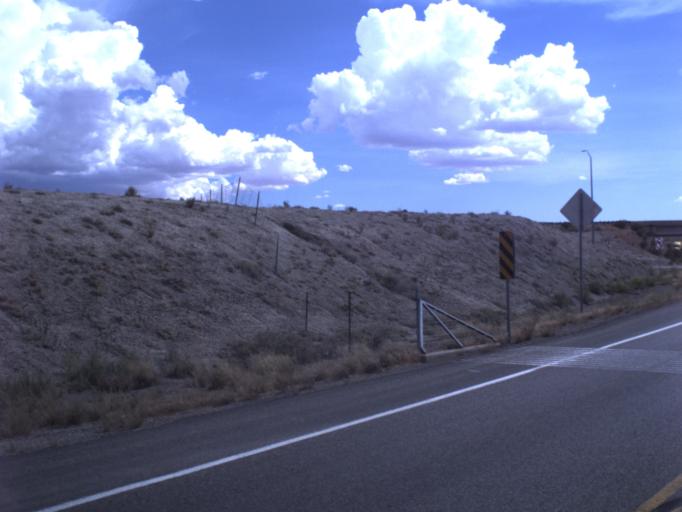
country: US
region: Utah
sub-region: Carbon County
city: East Carbon City
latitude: 38.9928
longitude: -110.1871
